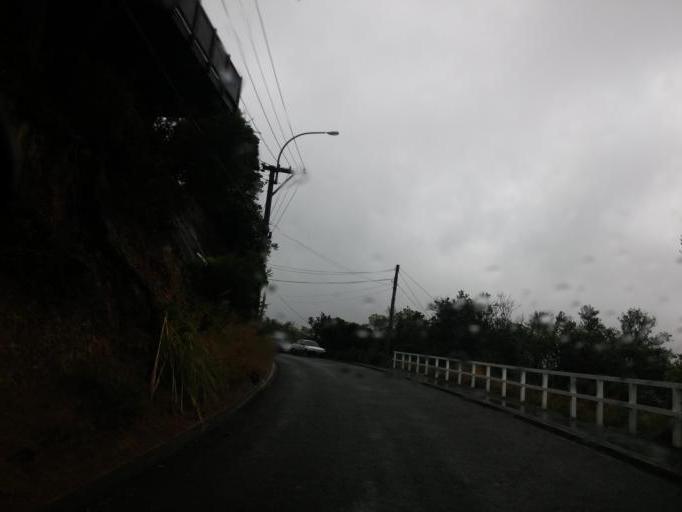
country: NZ
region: Wellington
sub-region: Wellington City
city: Wellington
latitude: -41.2595
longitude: 174.7842
